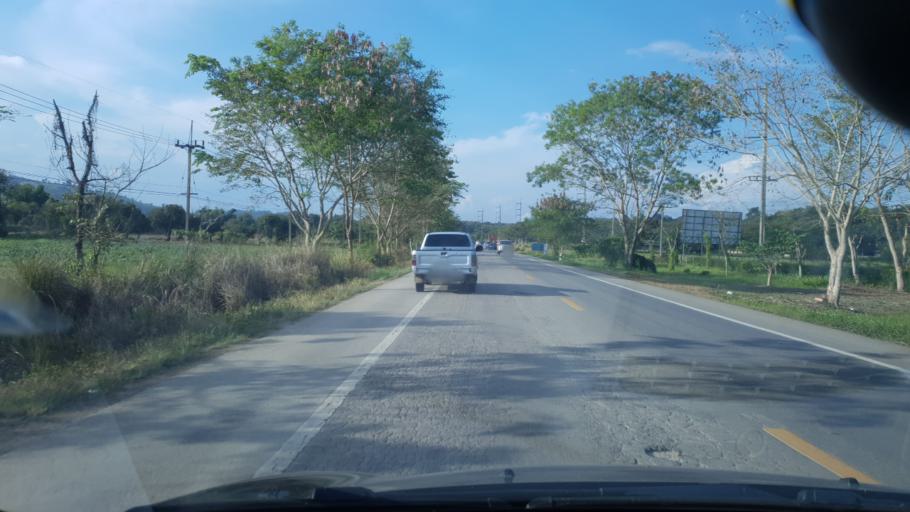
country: TH
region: Chiang Rai
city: Wiang Pa Pao
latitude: 19.3986
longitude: 99.5021
